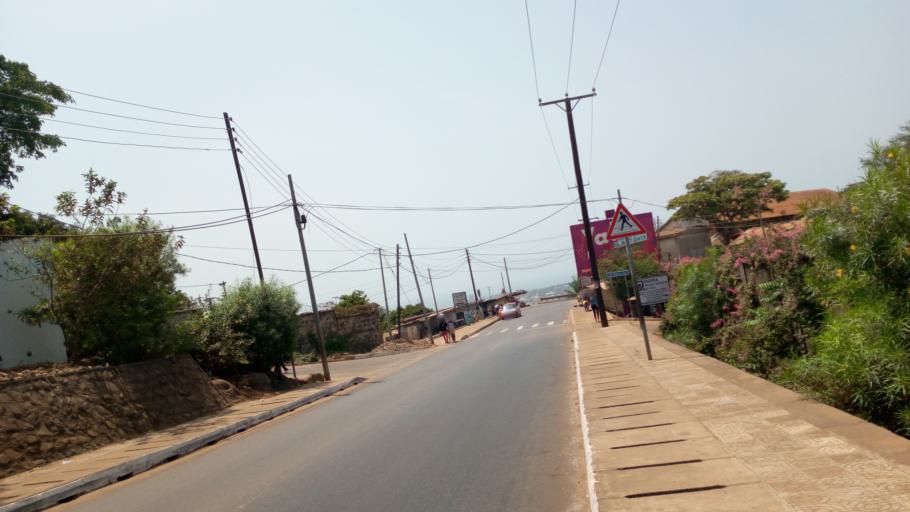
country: SL
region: Western Area
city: Freetown
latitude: 8.4805
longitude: -13.2648
